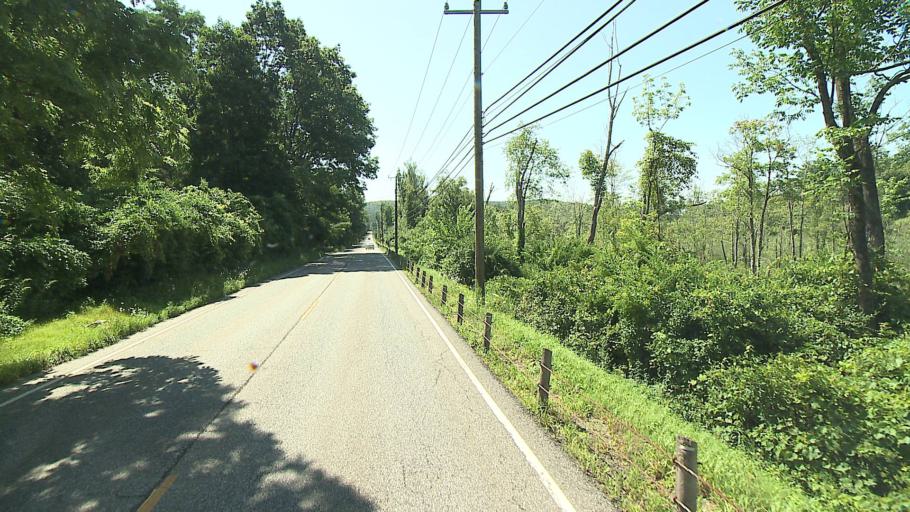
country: US
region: Connecticut
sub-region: Litchfield County
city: Kent
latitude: 41.8690
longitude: -73.4644
